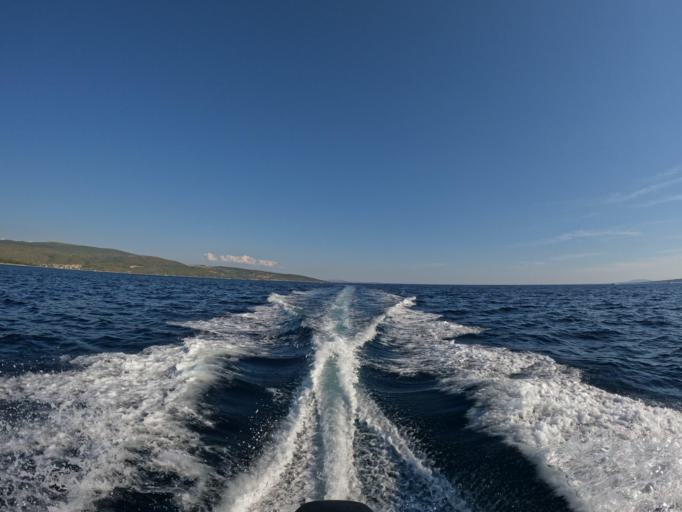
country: HR
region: Primorsko-Goranska
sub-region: Grad Krk
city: Krk
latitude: 45.0163
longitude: 14.5856
